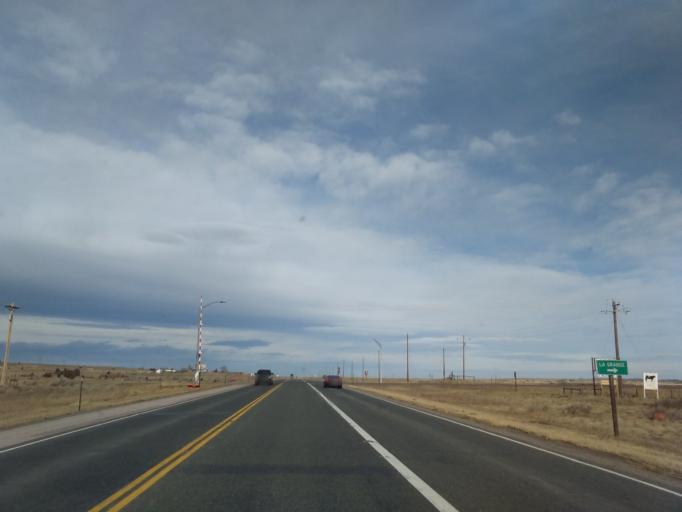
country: US
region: Wyoming
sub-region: Goshen County
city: Torrington
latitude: 41.6449
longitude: -104.2407
